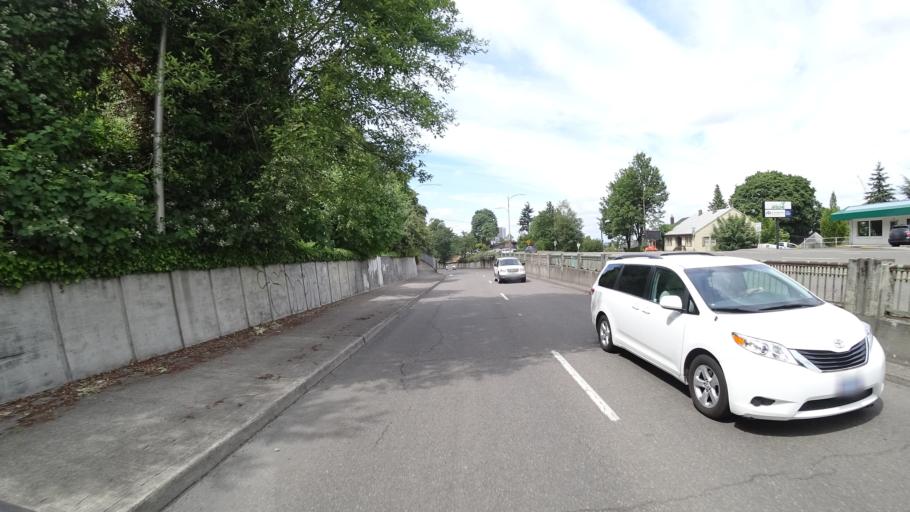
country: US
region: Oregon
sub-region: Multnomah County
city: Portland
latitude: 45.4940
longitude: -122.6773
